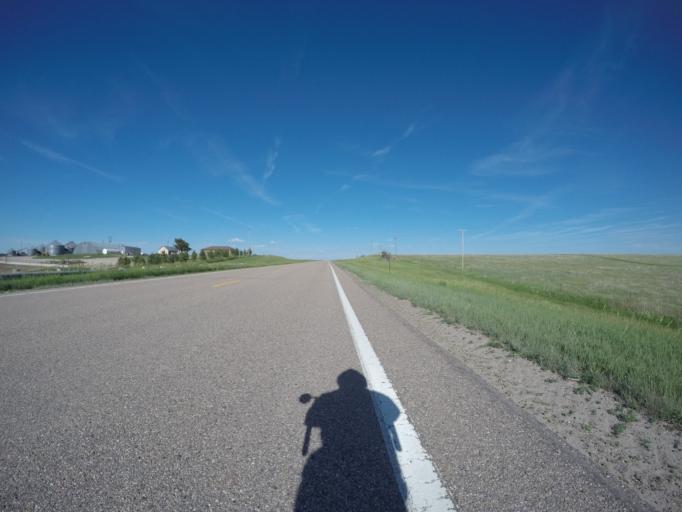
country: US
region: Kansas
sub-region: Cheyenne County
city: Saint Francis
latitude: 39.7567
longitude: -102.0147
